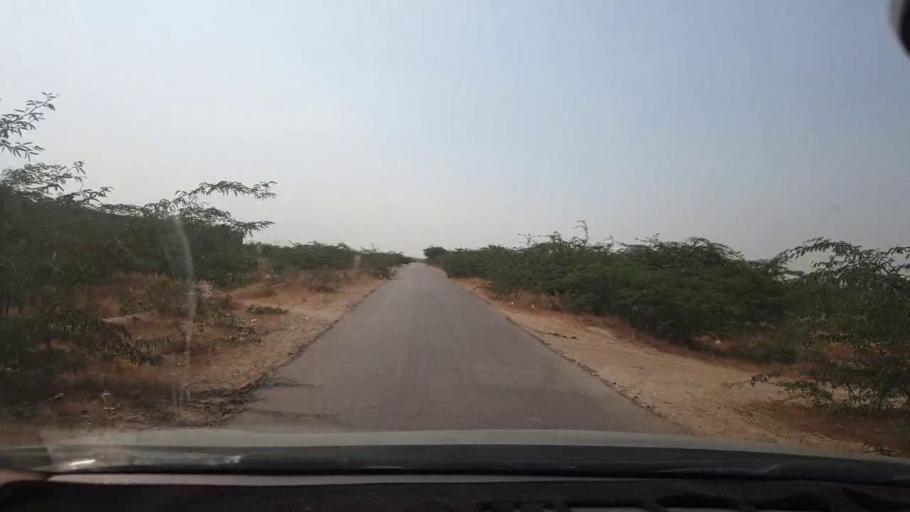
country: PK
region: Sindh
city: Malir Cantonment
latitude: 25.1275
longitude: 67.2254
